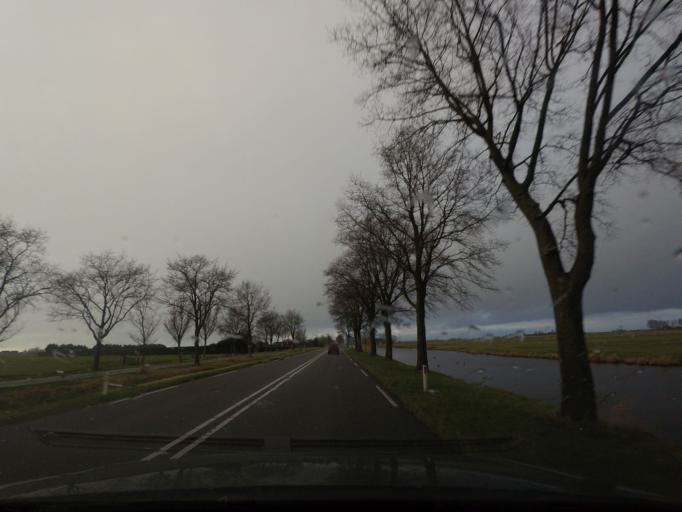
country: NL
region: North Holland
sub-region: Gemeente Edam-Volendam
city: Edam
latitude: 52.5300
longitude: 5.0352
